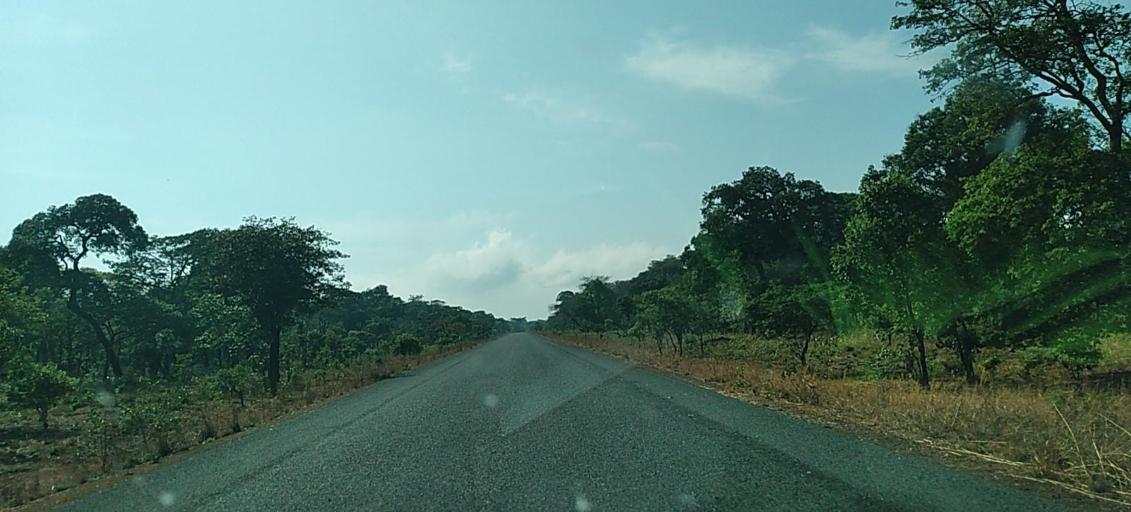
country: ZM
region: North-Western
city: Mwinilunga
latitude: -11.7332
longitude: 24.9746
